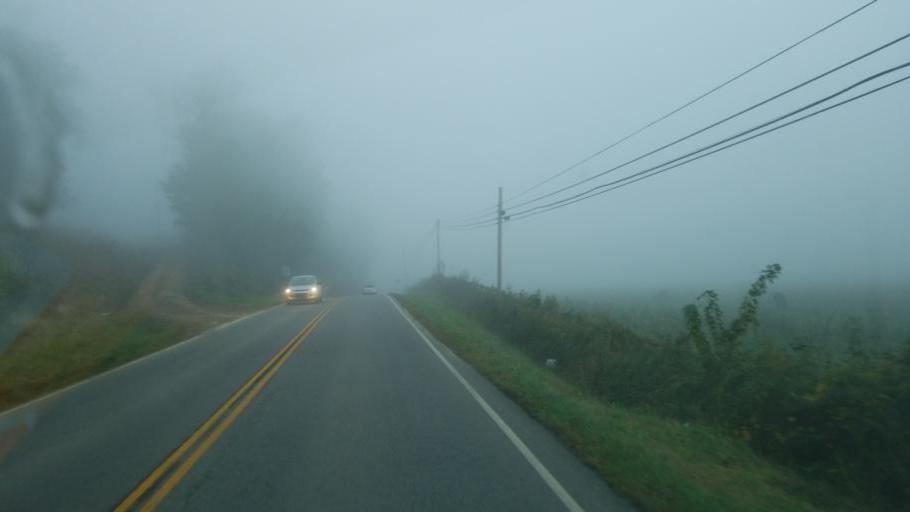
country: US
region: Ohio
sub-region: Scioto County
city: Portsmouth
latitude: 38.7006
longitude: -83.0366
